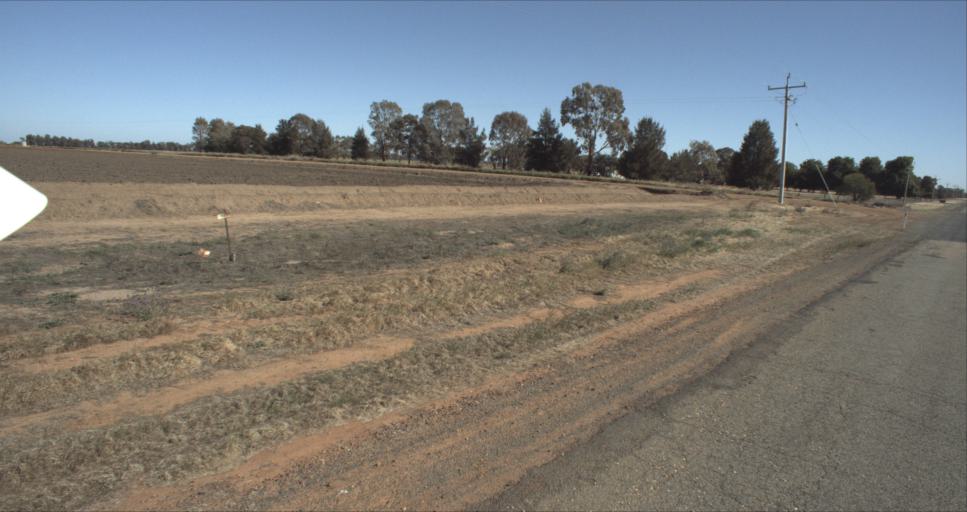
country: AU
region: New South Wales
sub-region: Leeton
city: Leeton
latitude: -34.5888
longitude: 146.2601
